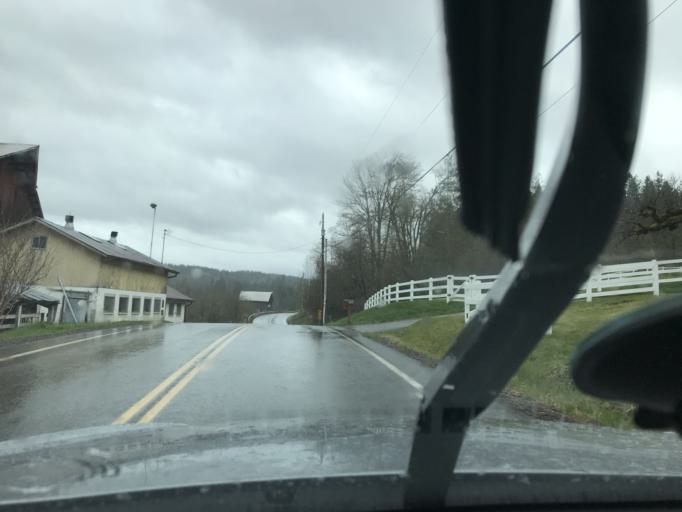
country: US
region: Washington
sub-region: King County
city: Ames Lake
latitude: 47.6680
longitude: -121.9741
